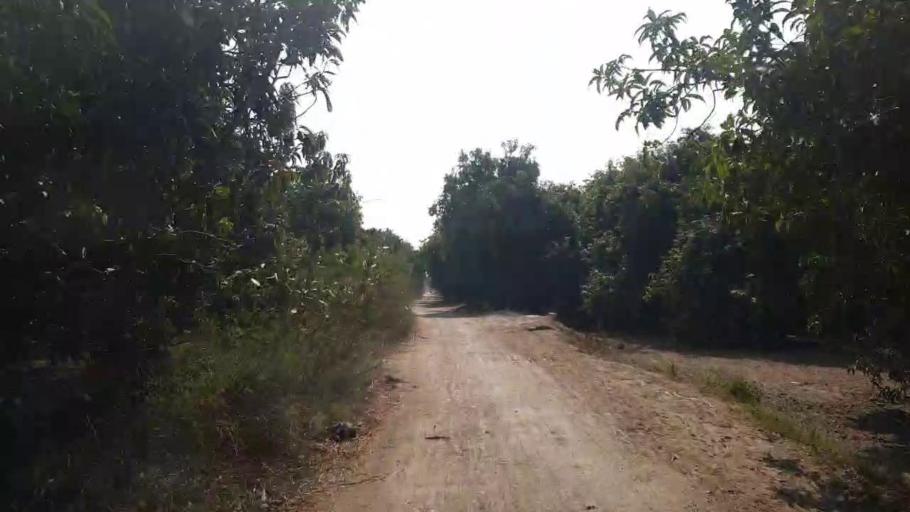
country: PK
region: Sindh
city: Tando Allahyar
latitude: 25.4728
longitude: 68.8500
